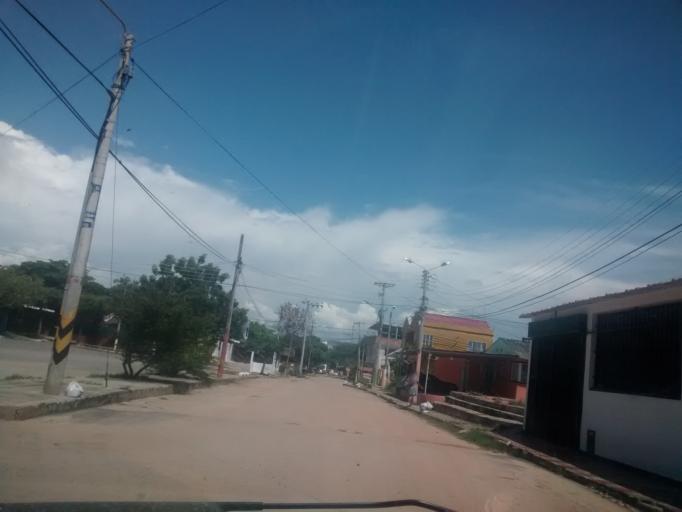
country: CO
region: Cundinamarca
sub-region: Girardot
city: Girardot City
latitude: 4.3125
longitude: -74.8030
